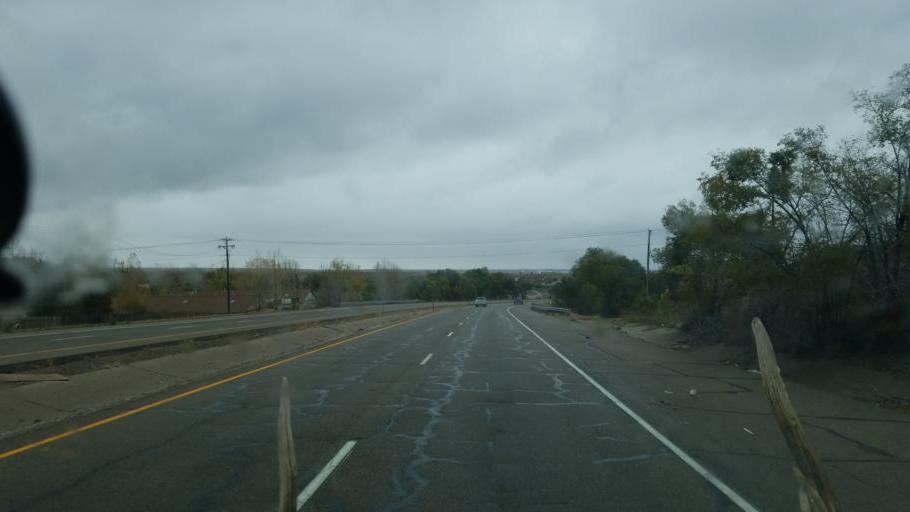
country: US
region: Colorado
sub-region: Pueblo County
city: Pueblo
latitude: 38.2862
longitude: -104.5827
